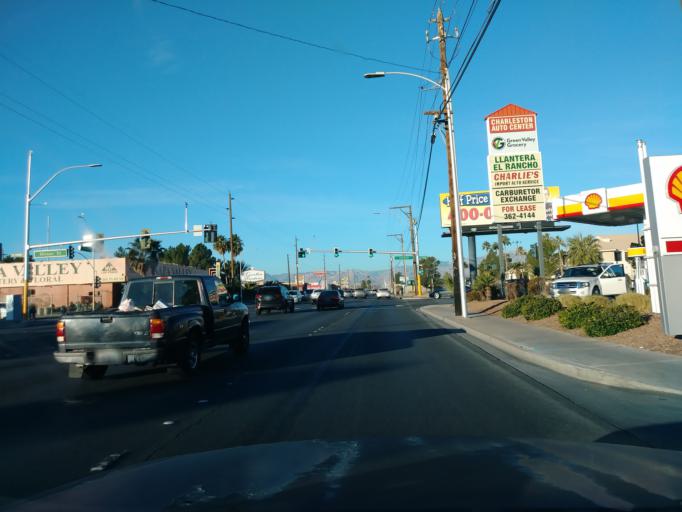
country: US
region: Nevada
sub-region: Clark County
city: Las Vegas
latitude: 36.1592
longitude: -115.1947
